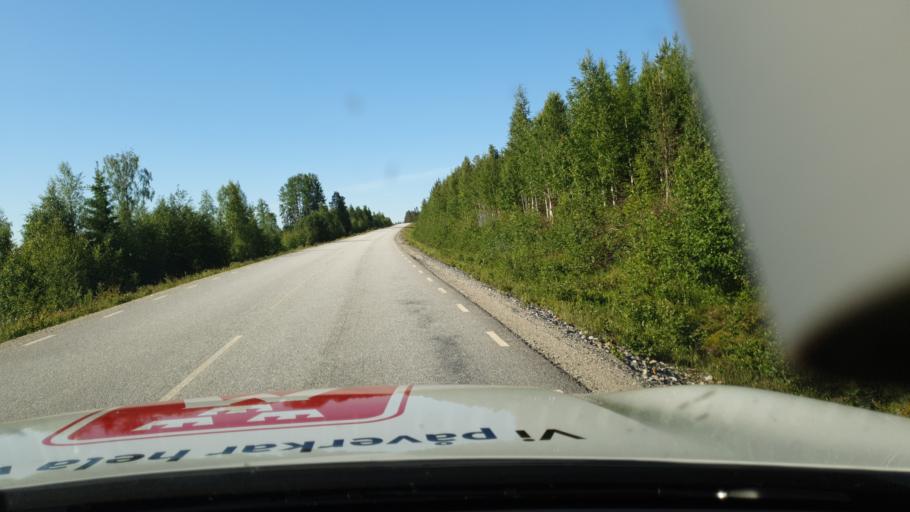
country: SE
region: Vaesterbotten
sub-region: Bjurholms Kommun
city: Bjurholm
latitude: 64.1840
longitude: 19.4024
